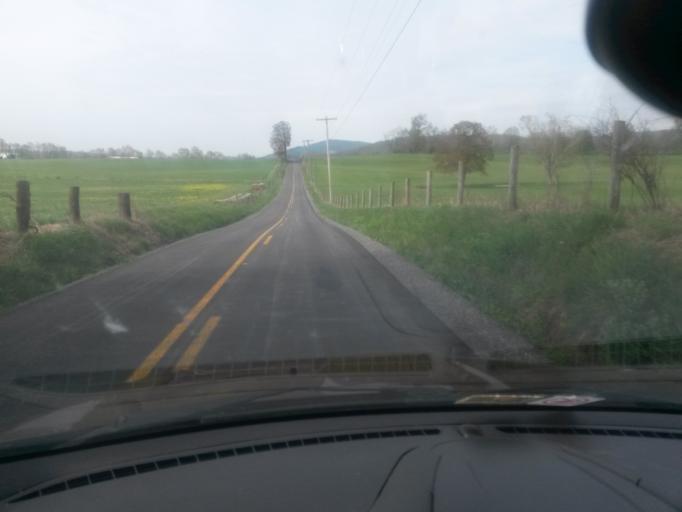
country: US
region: West Virginia
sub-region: Pocahontas County
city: Marlinton
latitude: 38.1149
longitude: -80.2152
